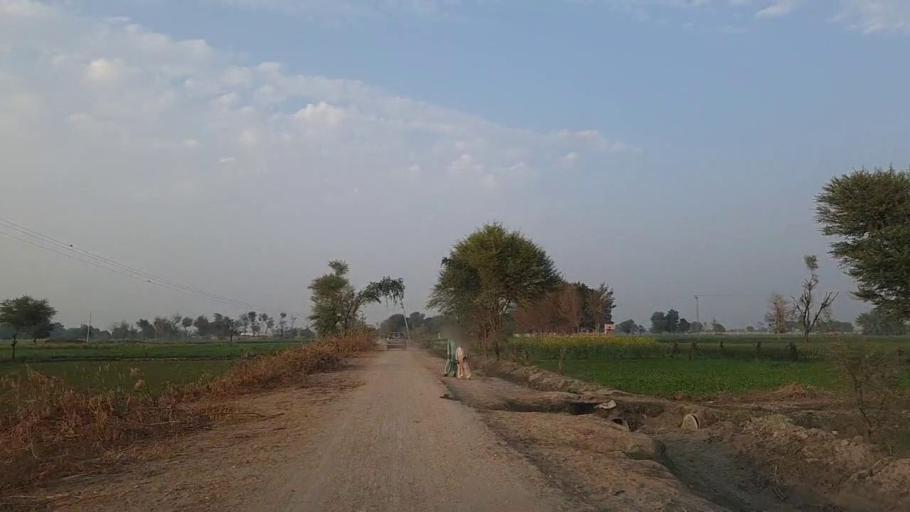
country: PK
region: Sindh
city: Jam Sahib
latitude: 26.3182
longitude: 68.6091
